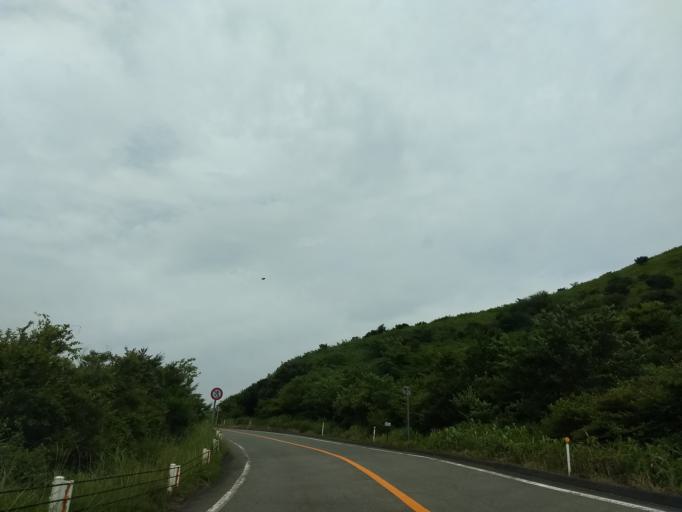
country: JP
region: Kanagawa
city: Hakone
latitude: 35.2319
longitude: 138.9774
